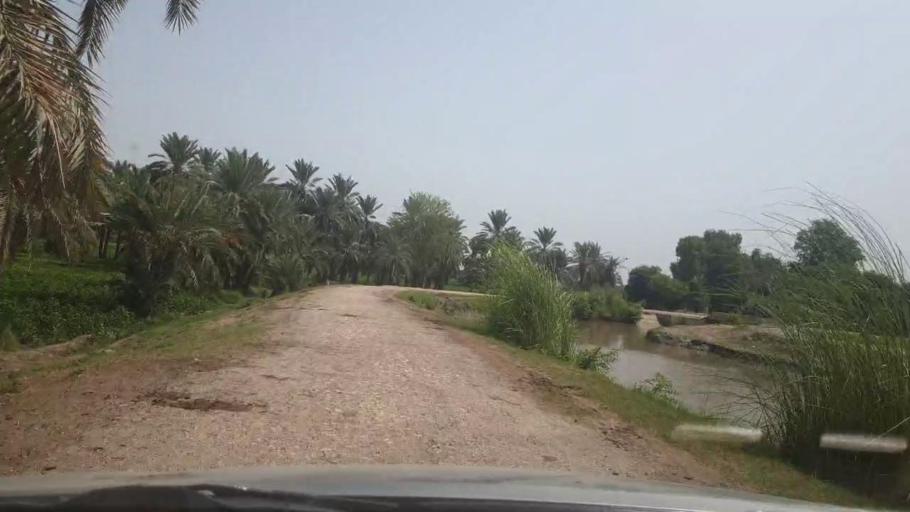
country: PK
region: Sindh
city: Pano Aqil
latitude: 27.8831
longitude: 69.1258
